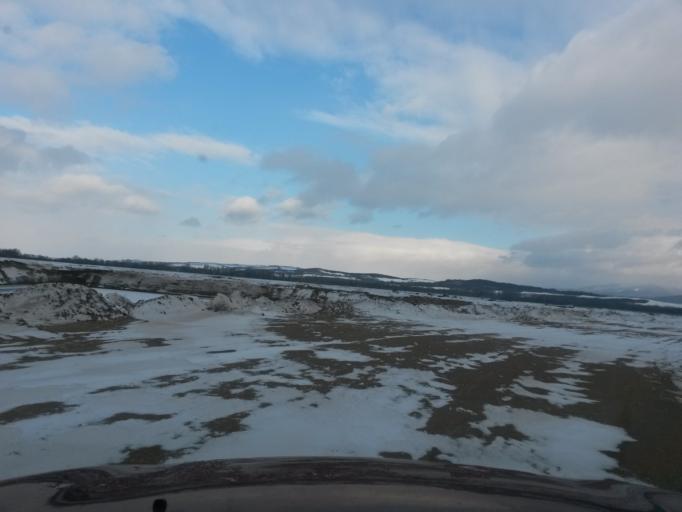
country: SK
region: Kosicky
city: Kosice
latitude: 48.6313
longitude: 21.3365
